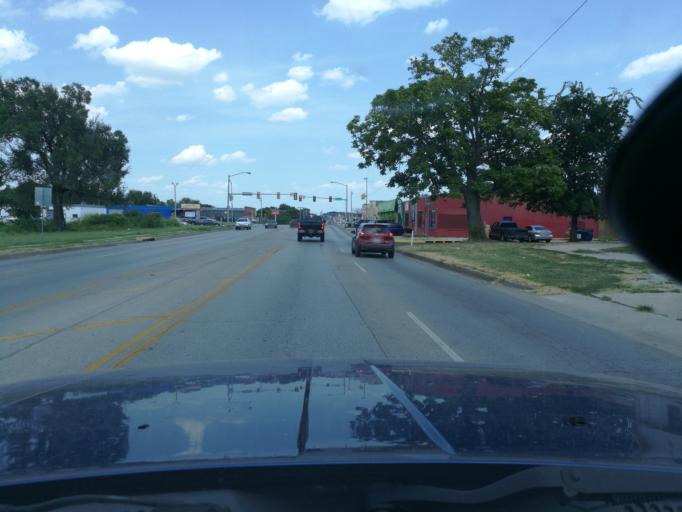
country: US
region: Oklahoma
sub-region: Oklahoma County
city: Oklahoma City
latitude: 35.4207
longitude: -97.5174
